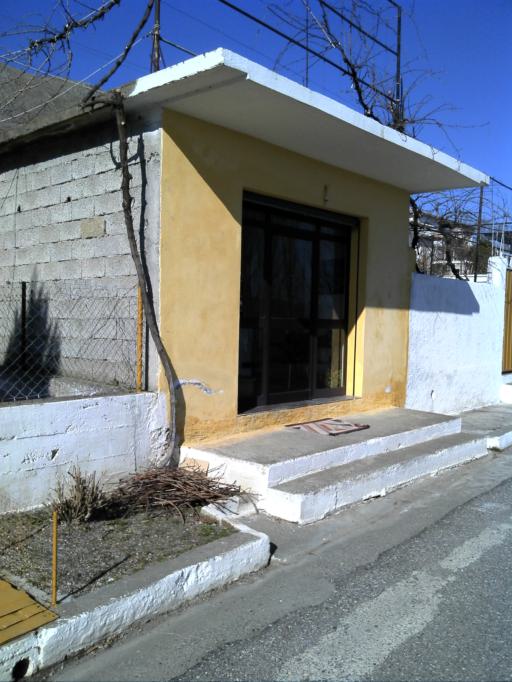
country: AL
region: Shkoder
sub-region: Rrethi i Shkodres
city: Berdica e Madhe
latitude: 42.0339
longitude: 19.4777
